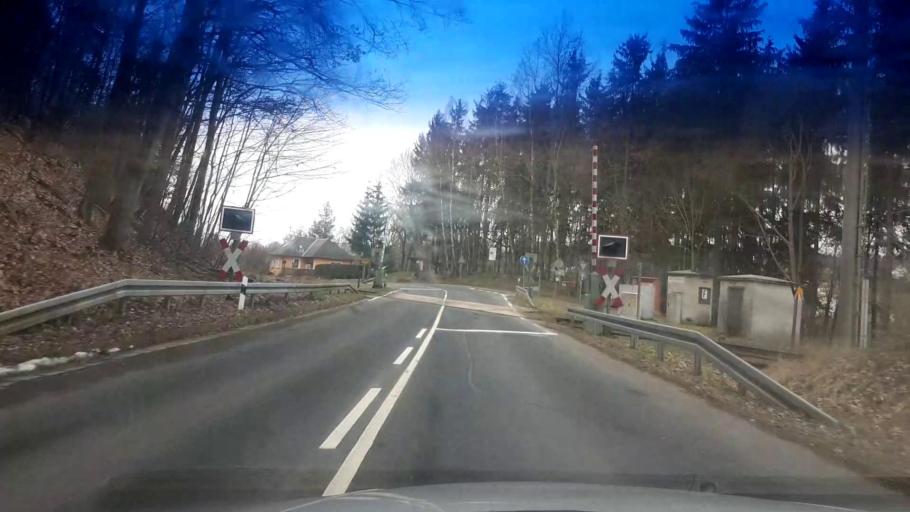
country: DE
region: Bavaria
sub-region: Upper Franconia
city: Schirnding
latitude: 50.0826
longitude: 12.2323
